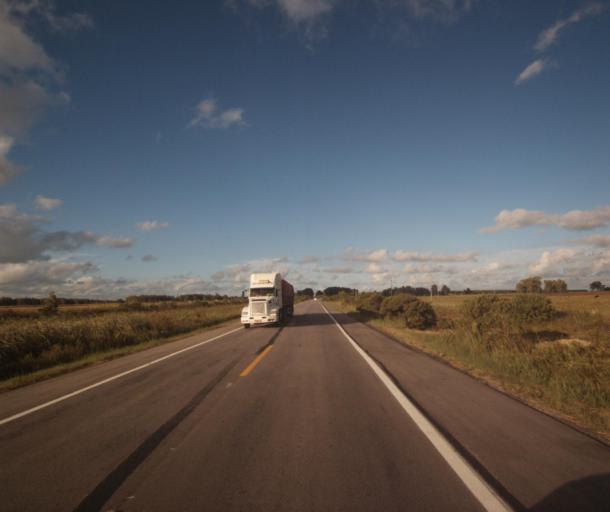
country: BR
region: Rio Grande do Sul
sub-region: Rio Grande
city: Rio Grande
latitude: -32.1308
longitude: -52.3702
